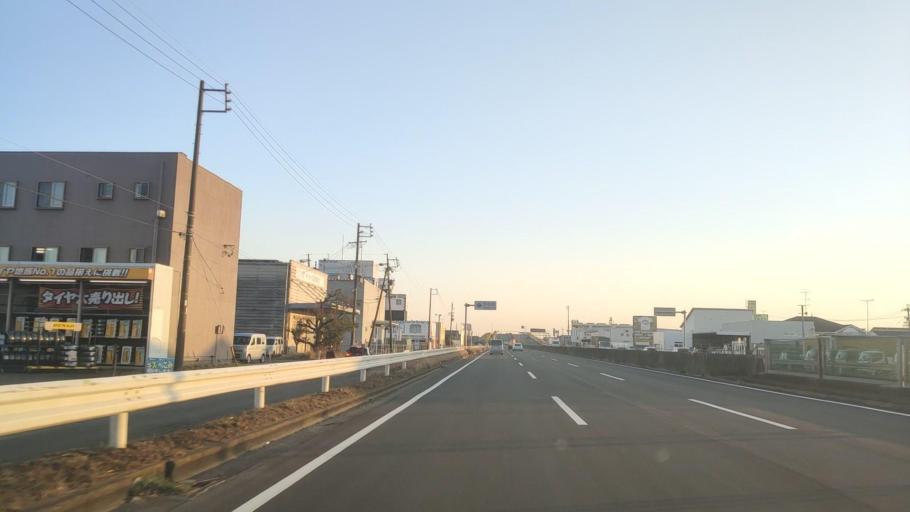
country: JP
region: Gifu
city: Kasamatsucho
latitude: 35.3805
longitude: 136.7845
